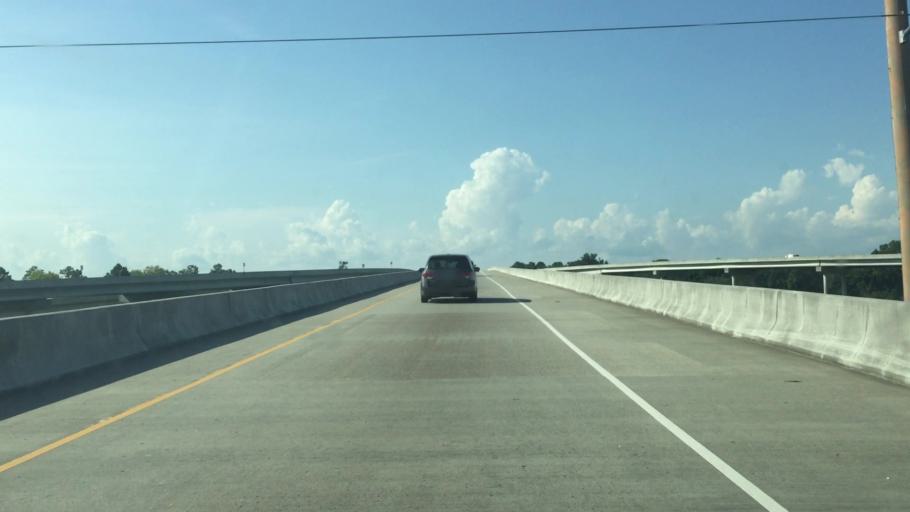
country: US
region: South Carolina
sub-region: Horry County
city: North Myrtle Beach
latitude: 33.7870
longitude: -78.7759
